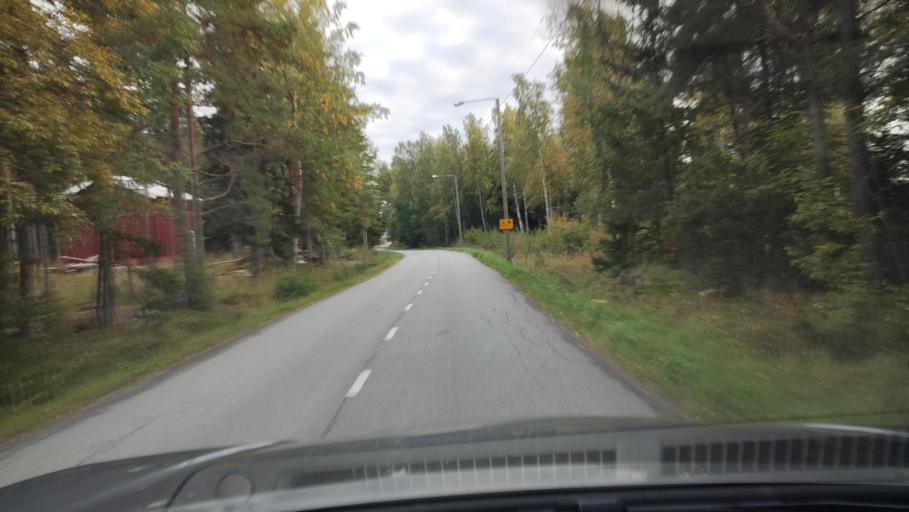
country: FI
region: Ostrobothnia
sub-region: Sydosterbotten
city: Kristinestad
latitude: 62.2590
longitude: 21.3836
